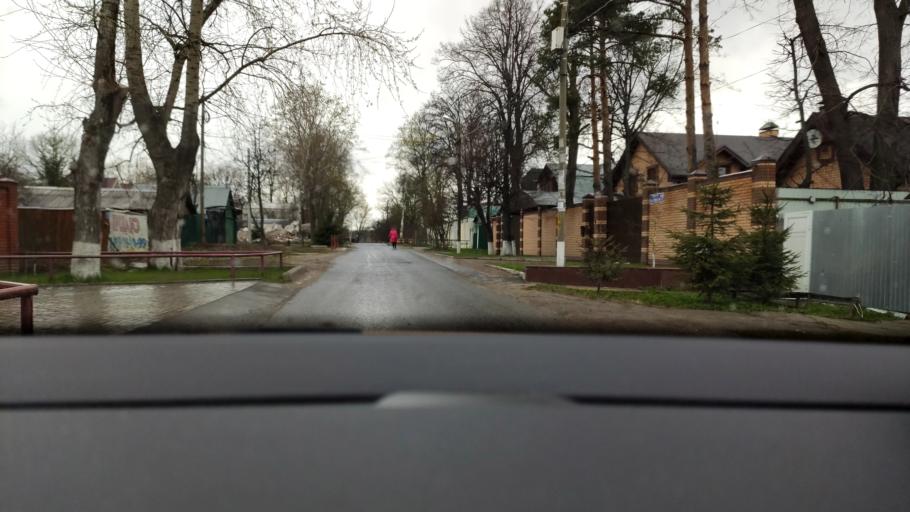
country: RU
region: Moskovskaya
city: Reutov
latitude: 55.7730
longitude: 37.8885
